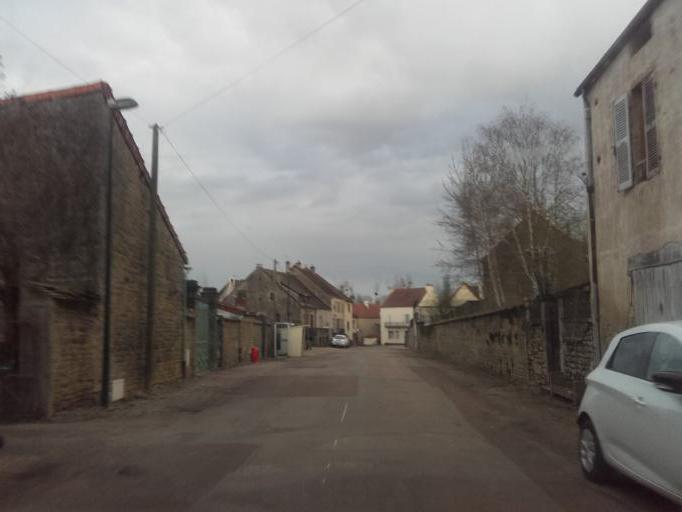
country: FR
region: Bourgogne
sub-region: Departement de la Cote-d'Or
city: Nolay
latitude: 46.9139
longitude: 4.6352
